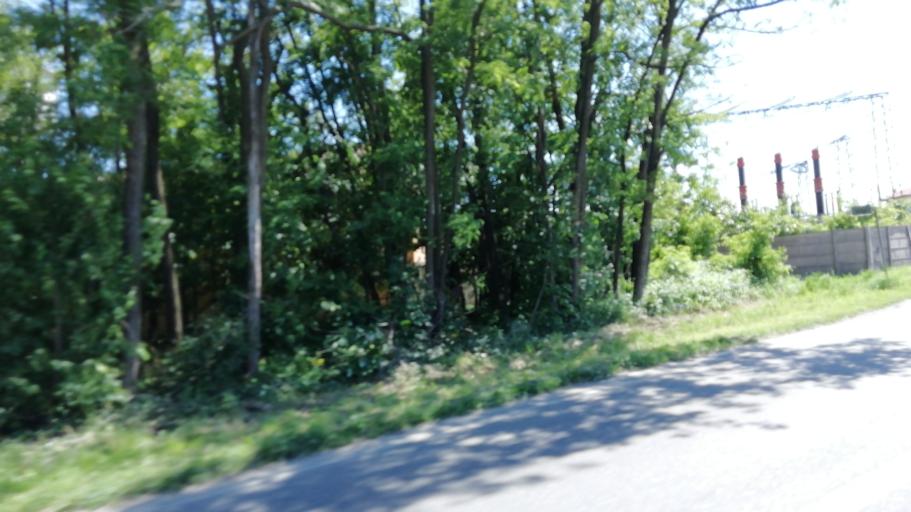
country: IT
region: Lombardy
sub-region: Provincia di Varese
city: Lonate Pozzolo
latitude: 45.6045
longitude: 8.7493
